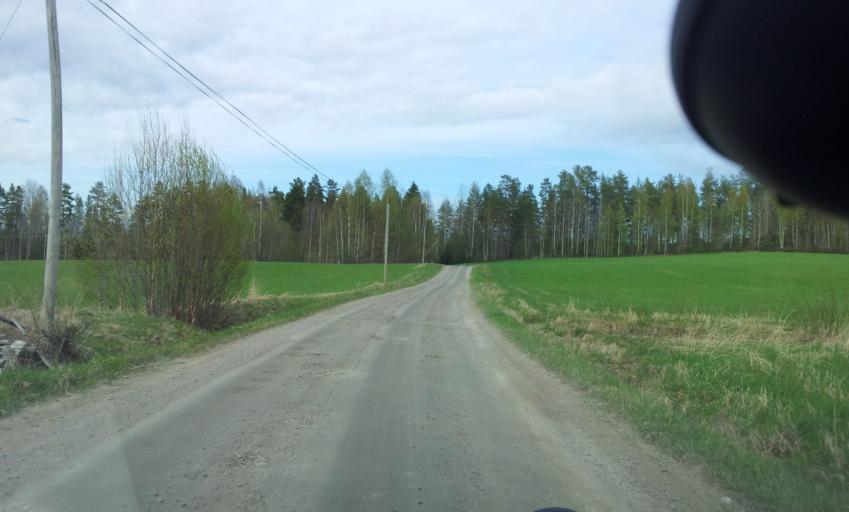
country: SE
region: Gaevleborg
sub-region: Ljusdals Kommun
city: Farila
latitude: 61.7954
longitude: 15.9054
